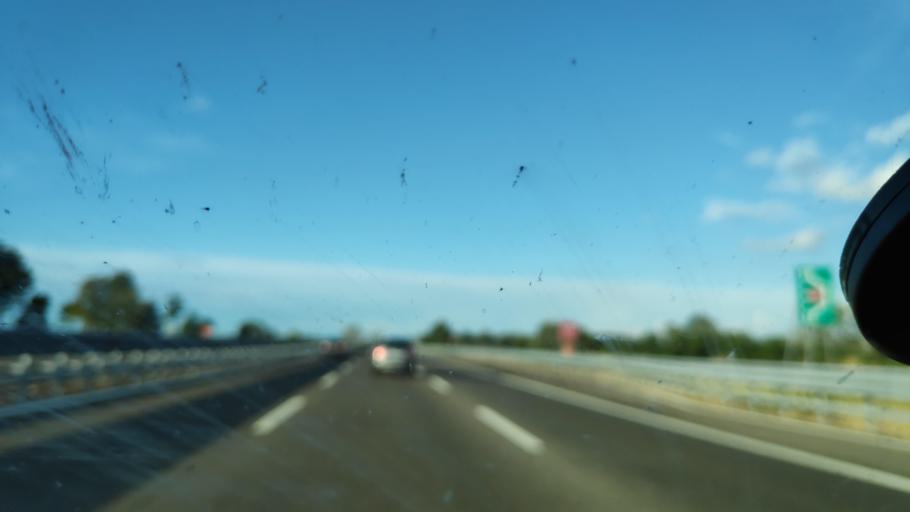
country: IT
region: Piedmont
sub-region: Provincia di Alessandria
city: Castelnuovo Scrivia
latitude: 44.9463
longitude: 8.8605
